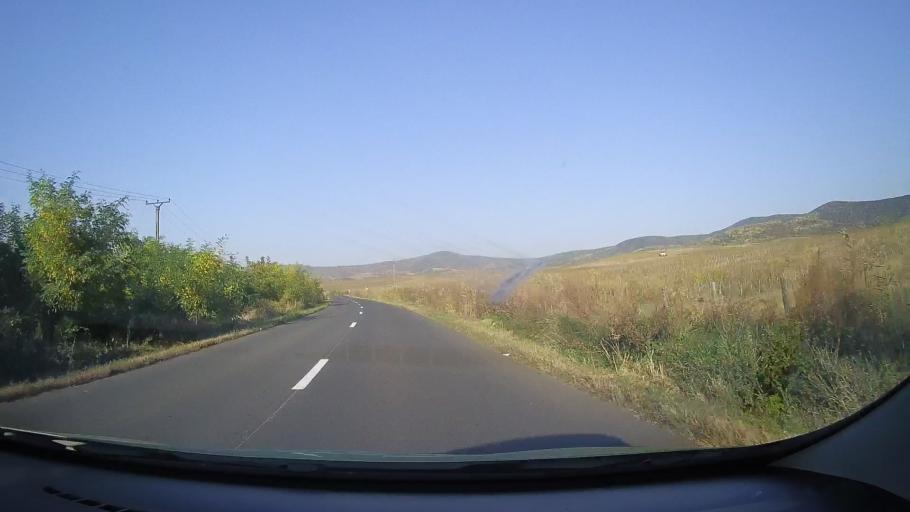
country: RO
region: Arad
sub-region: Comuna Siria
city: Siria
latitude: 46.2276
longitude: 21.6338
